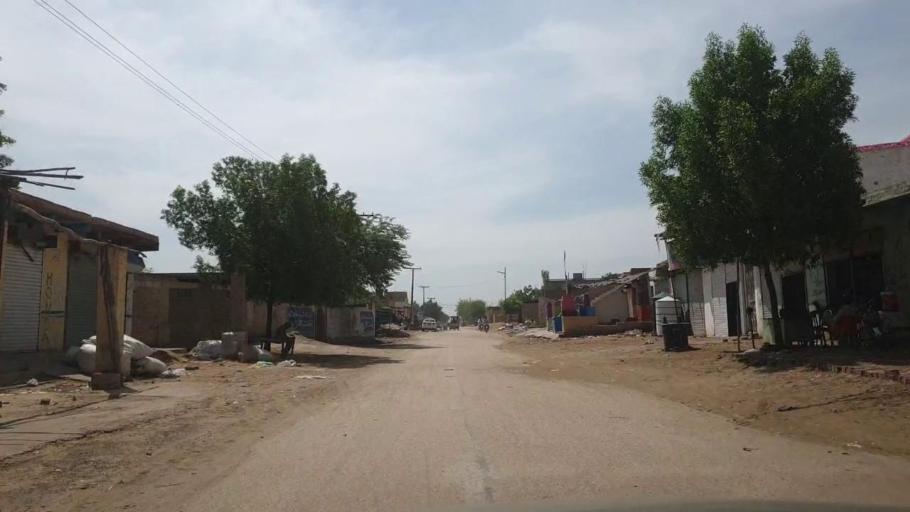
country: PK
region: Sindh
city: Kot Diji
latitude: 27.1584
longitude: 68.9591
